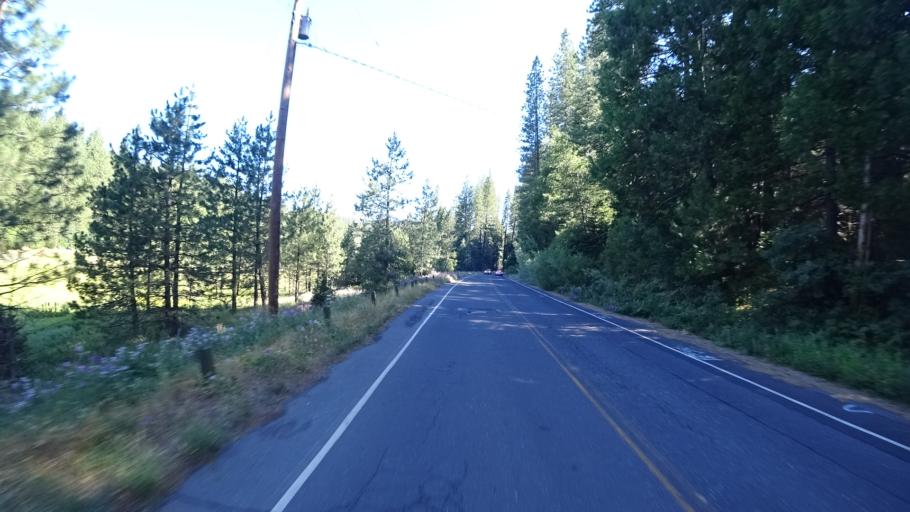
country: US
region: California
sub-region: Calaveras County
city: Arnold
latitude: 38.2601
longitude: -120.3431
